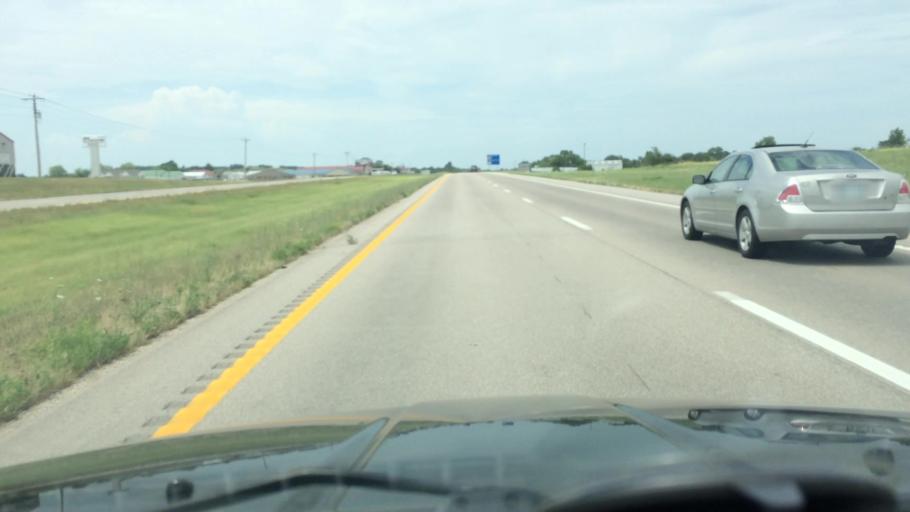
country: US
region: Missouri
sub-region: Polk County
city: Bolivar
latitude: 37.5578
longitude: -93.3895
